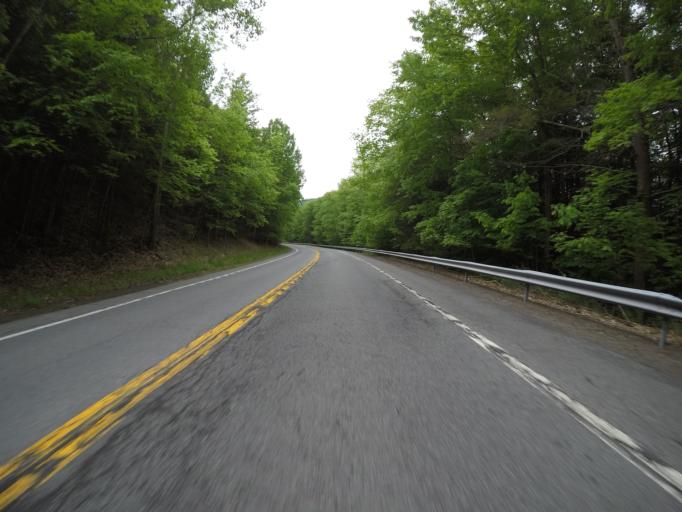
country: US
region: New York
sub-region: Sullivan County
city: Livingston Manor
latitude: 42.0792
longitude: -74.8858
